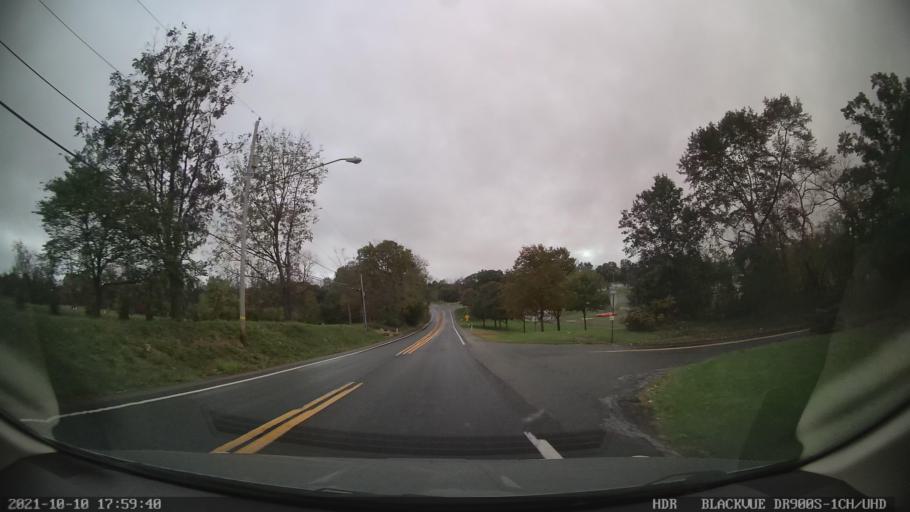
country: US
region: Pennsylvania
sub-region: Lehigh County
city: Egypt
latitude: 40.6394
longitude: -75.5563
